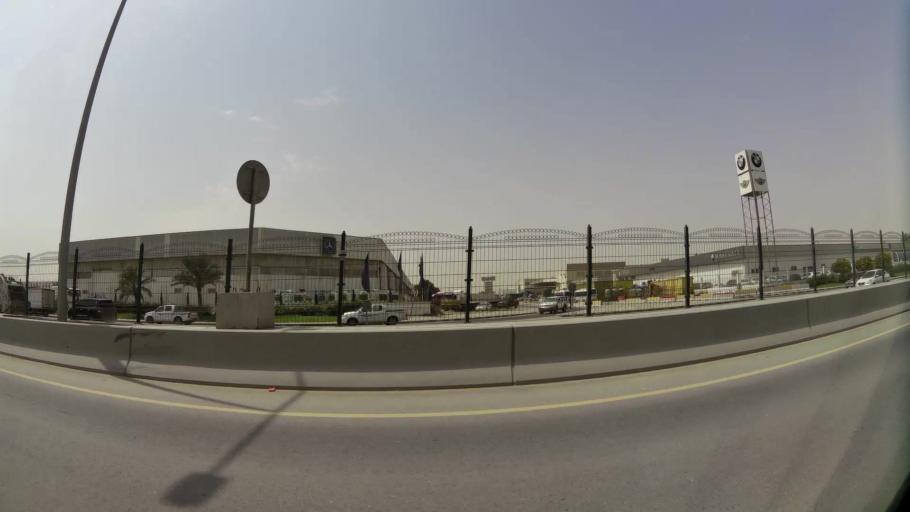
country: QA
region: Baladiyat ar Rayyan
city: Ar Rayyan
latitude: 25.2195
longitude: 51.4363
